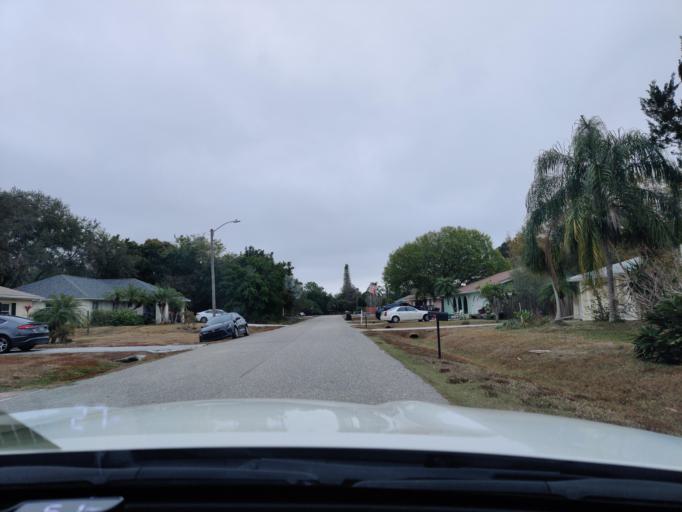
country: US
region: Florida
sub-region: Sarasota County
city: South Venice
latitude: 27.0387
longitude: -82.4041
